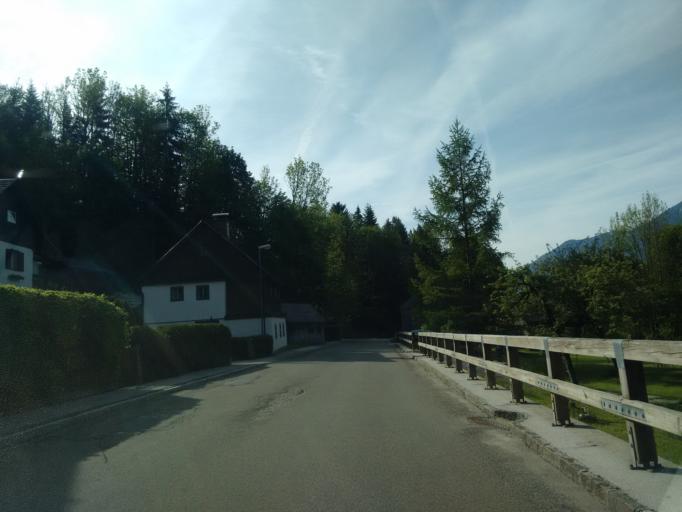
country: AT
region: Styria
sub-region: Politischer Bezirk Liezen
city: Altaussee
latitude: 47.6451
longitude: 13.7614
